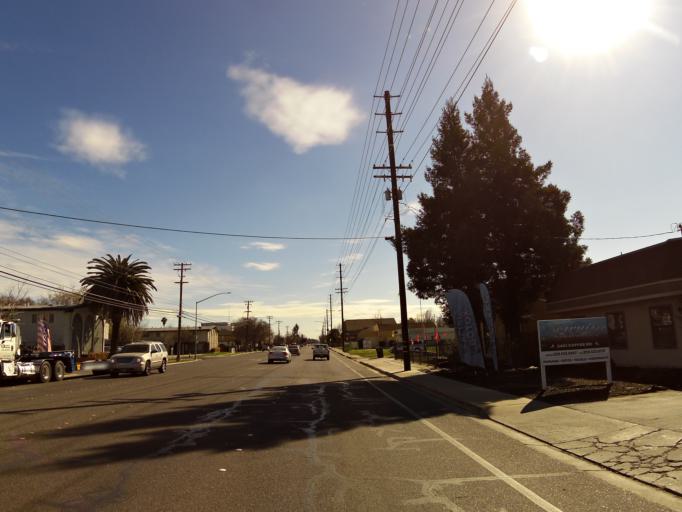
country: US
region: California
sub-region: Stanislaus County
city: Modesto
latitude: 37.6763
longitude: -120.9759
